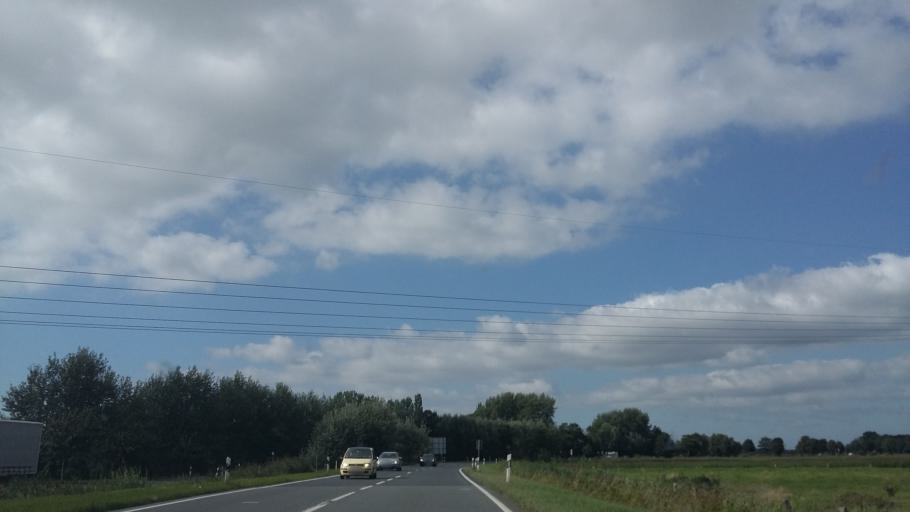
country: DE
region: Lower Saxony
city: Loxstedt
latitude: 53.4687
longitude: 8.5980
